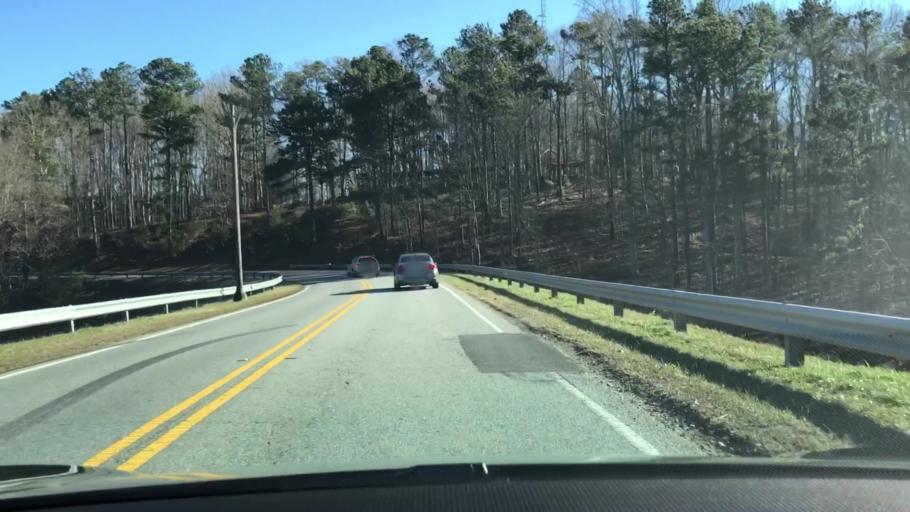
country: US
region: Georgia
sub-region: Gwinnett County
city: Sugar Hill
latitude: 34.1588
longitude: -84.0729
